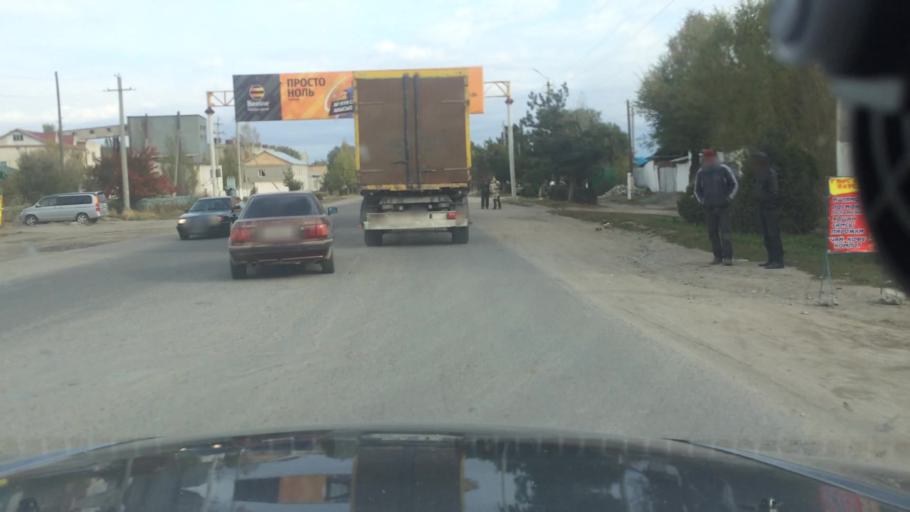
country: KG
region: Ysyk-Koel
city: Karakol
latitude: 42.5132
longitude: 78.3858
